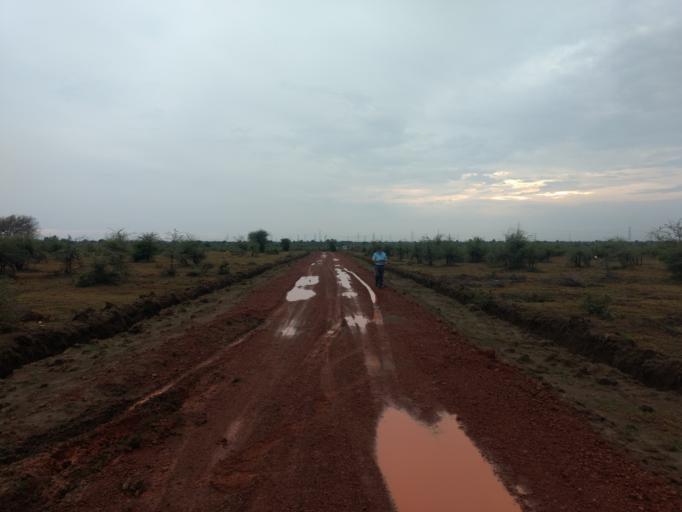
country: IN
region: Maharashtra
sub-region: Chandrapur
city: Chandrapur
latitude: 19.9730
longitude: 79.2144
